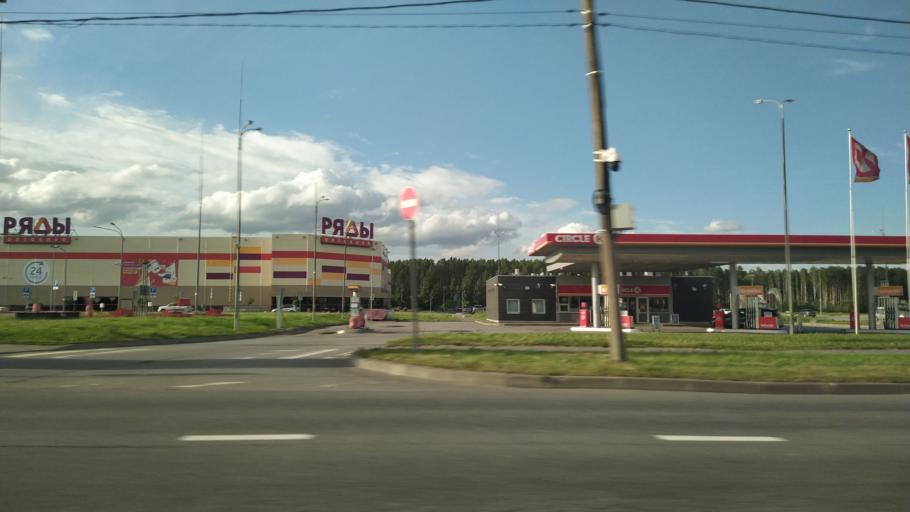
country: RU
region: St.-Petersburg
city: Krasnogvargeisky
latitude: 59.9884
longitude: 30.4660
